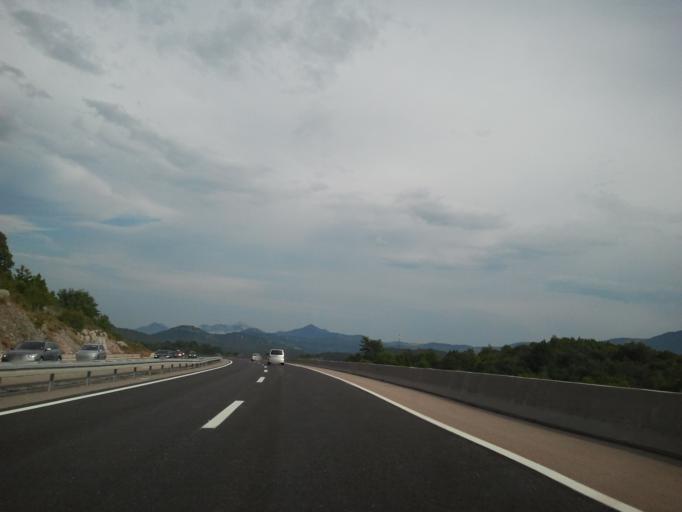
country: HR
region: Zadarska
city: Obrovac
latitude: 44.3342
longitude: 15.6556
